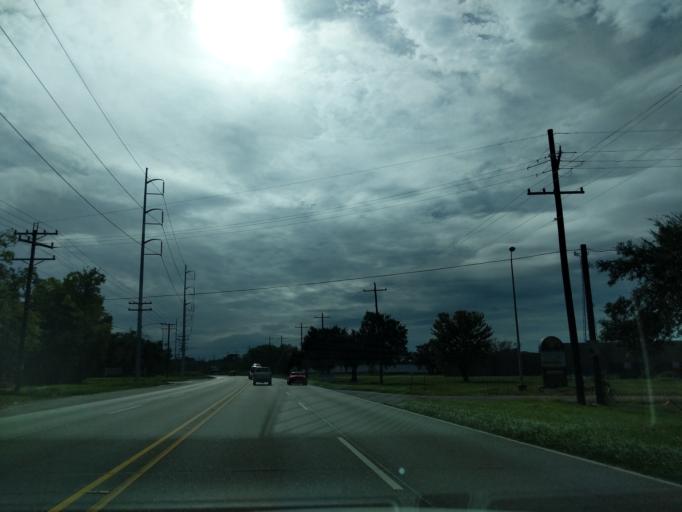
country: US
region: Louisiana
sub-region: Saint Bernard Parish
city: Chalmette
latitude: 30.0204
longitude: -89.9277
